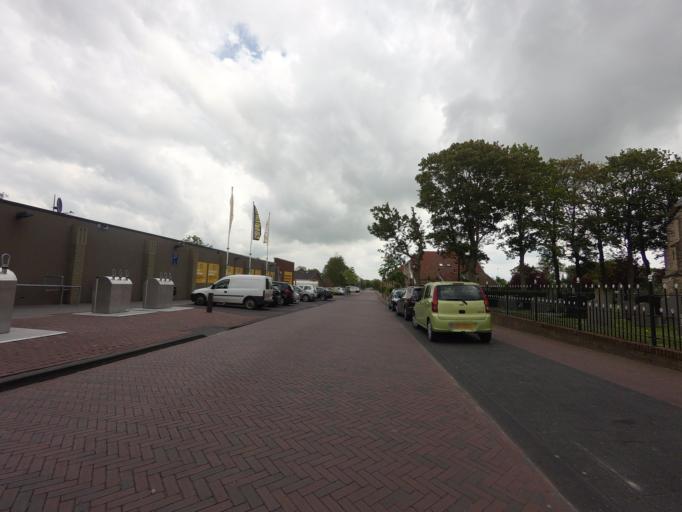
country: NL
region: Friesland
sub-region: Gemeente Littenseradiel
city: Wommels
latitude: 53.1085
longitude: 5.5882
